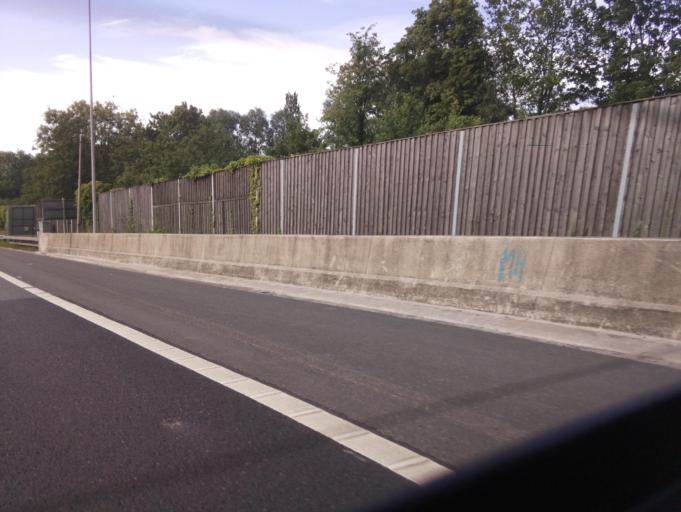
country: GB
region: England
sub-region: Manchester
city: Swinton
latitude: 53.4914
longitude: -2.3793
